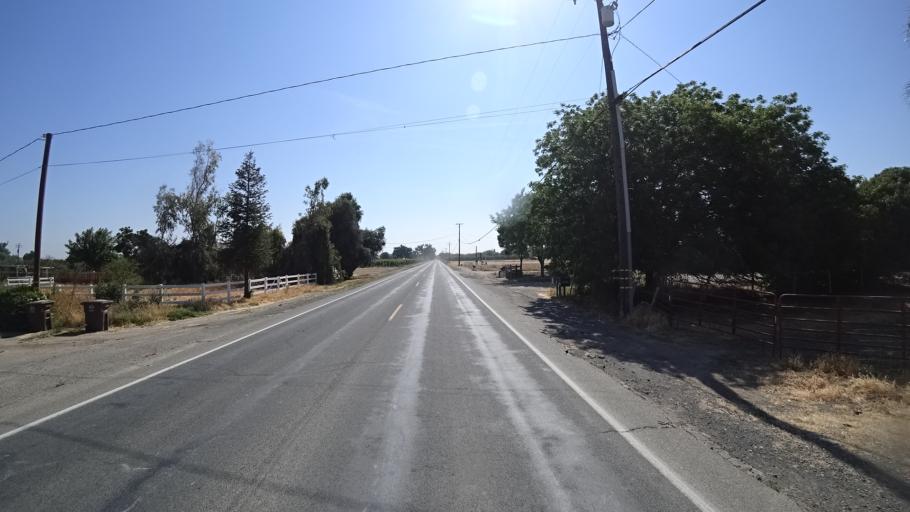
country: US
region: California
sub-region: Kings County
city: Lemoore
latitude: 36.3440
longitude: -119.8486
